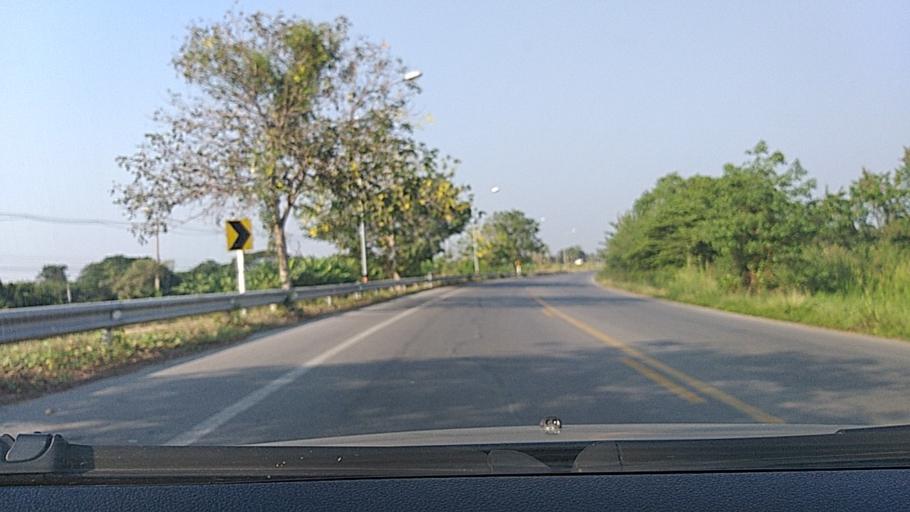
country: TH
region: Sing Buri
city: Phrom Buri
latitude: 14.8231
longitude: 100.4287
